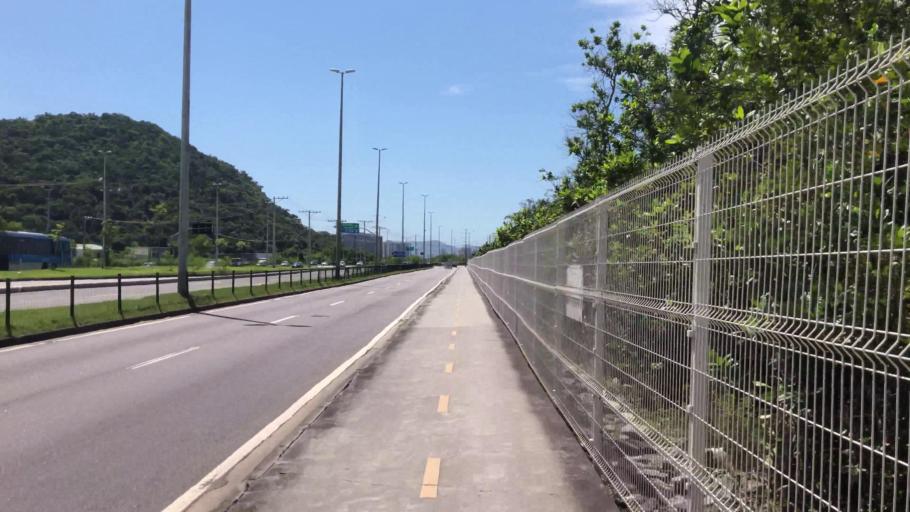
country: BR
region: Rio de Janeiro
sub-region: Nilopolis
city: Nilopolis
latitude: -22.9735
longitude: -43.3901
